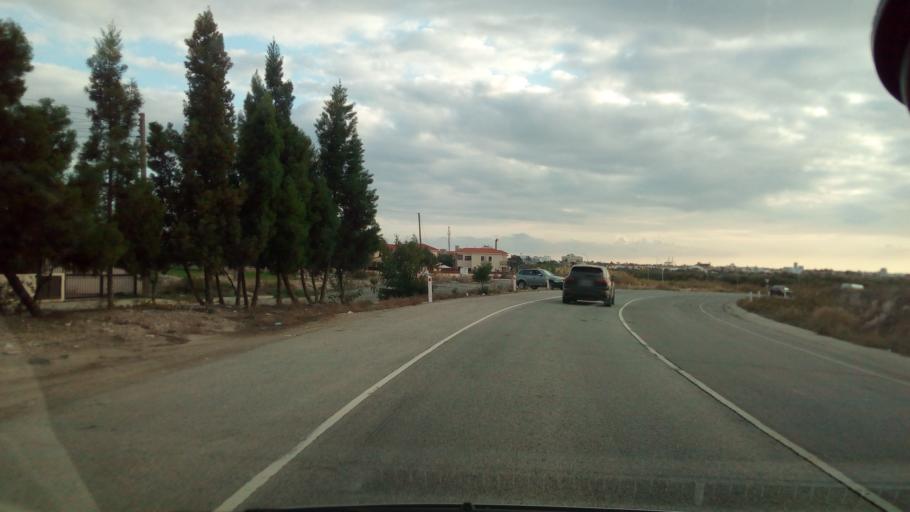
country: CY
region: Larnaka
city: Voroklini
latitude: 34.9714
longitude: 33.6574
